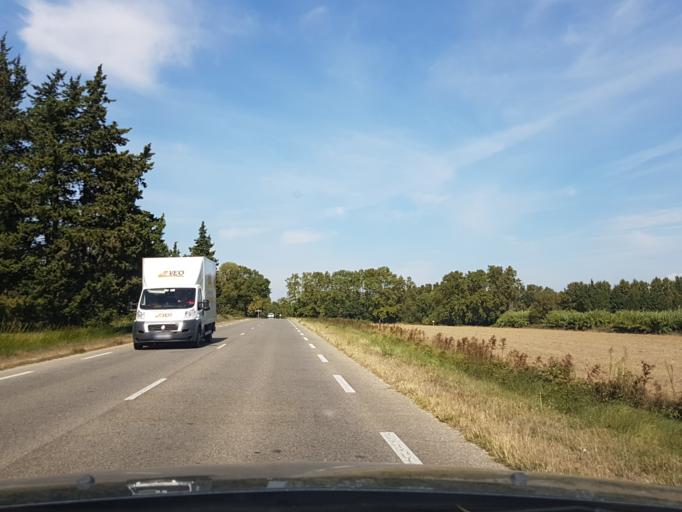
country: FR
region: Provence-Alpes-Cote d'Azur
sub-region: Departement des Bouches-du-Rhone
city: Noves
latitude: 43.8391
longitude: 4.8943
